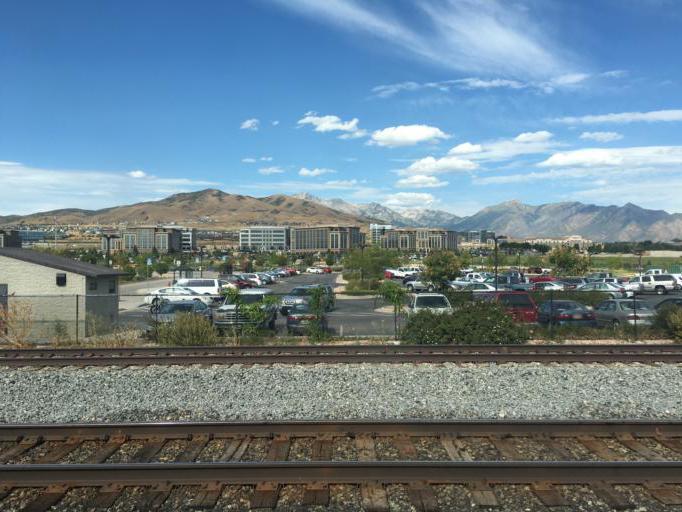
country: US
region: Utah
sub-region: Utah County
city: Lehi
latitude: 40.4250
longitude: -111.8960
